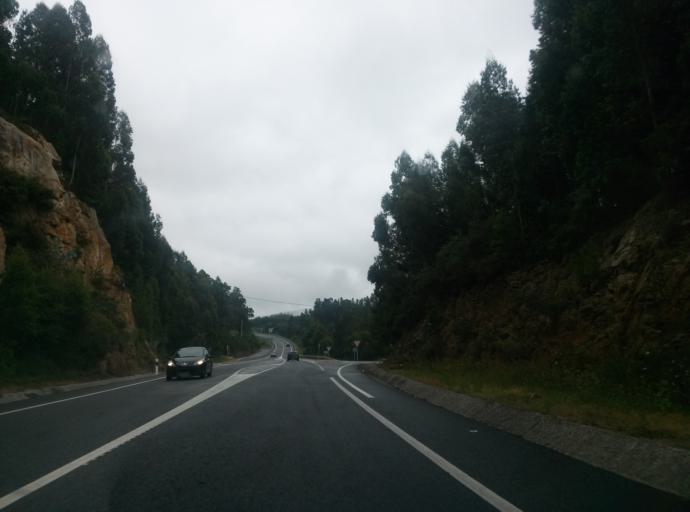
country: ES
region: Galicia
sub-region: Provincia de Lugo
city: Viveiro
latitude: 43.5713
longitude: -7.6396
